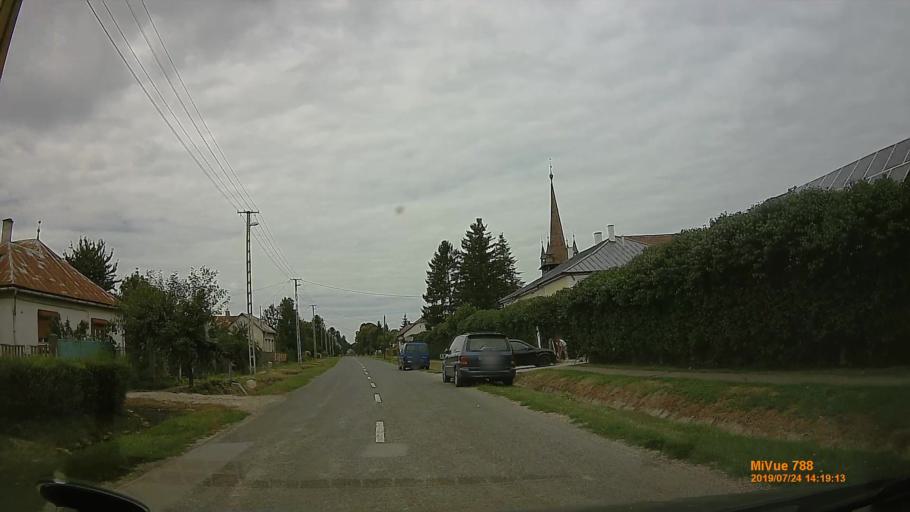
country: HU
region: Szabolcs-Szatmar-Bereg
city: Mandok
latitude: 48.3178
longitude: 22.2707
